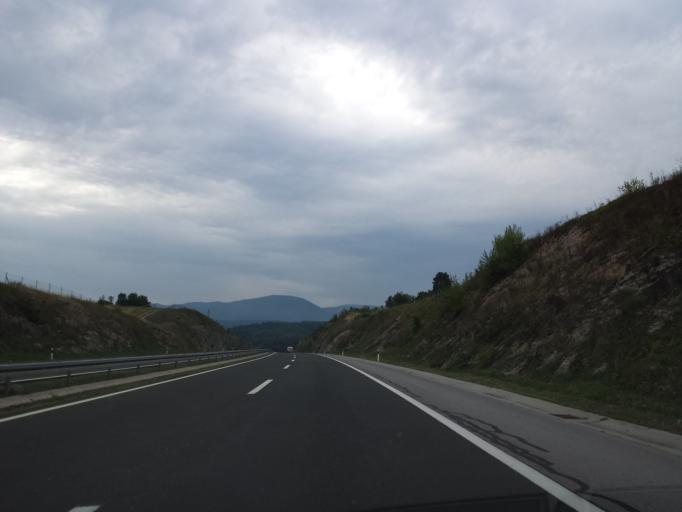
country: HR
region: Karlovacka
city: Ostarije
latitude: 45.1638
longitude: 15.2738
